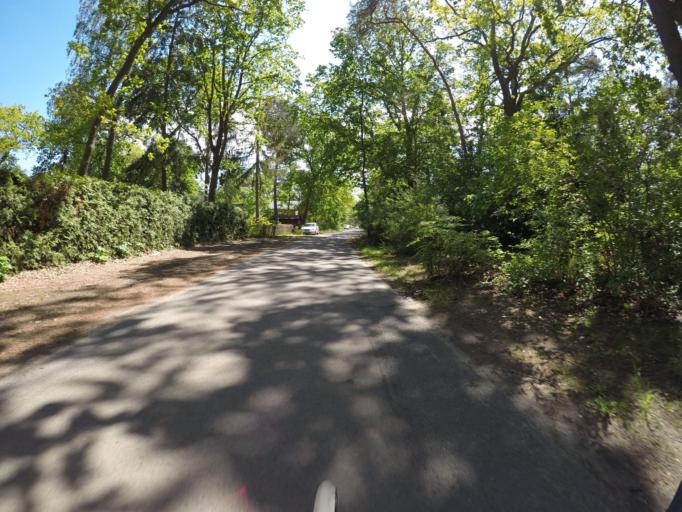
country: DE
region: Brandenburg
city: Werder
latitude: 52.3909
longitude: 12.9450
